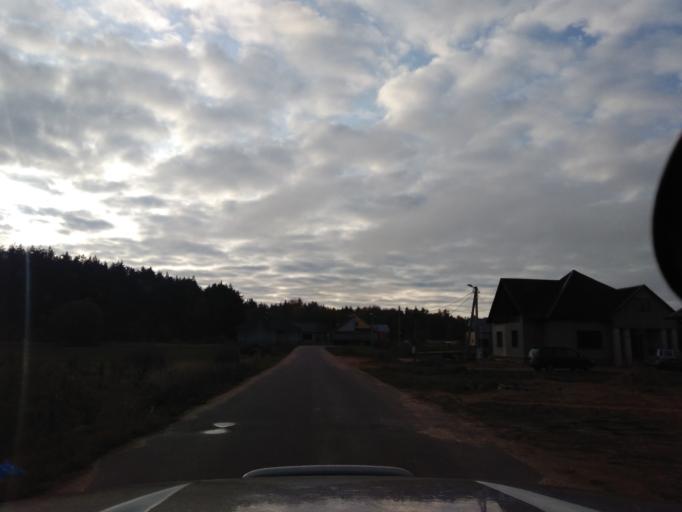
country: BY
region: Minsk
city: Kapyl'
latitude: 53.1630
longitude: 27.1031
